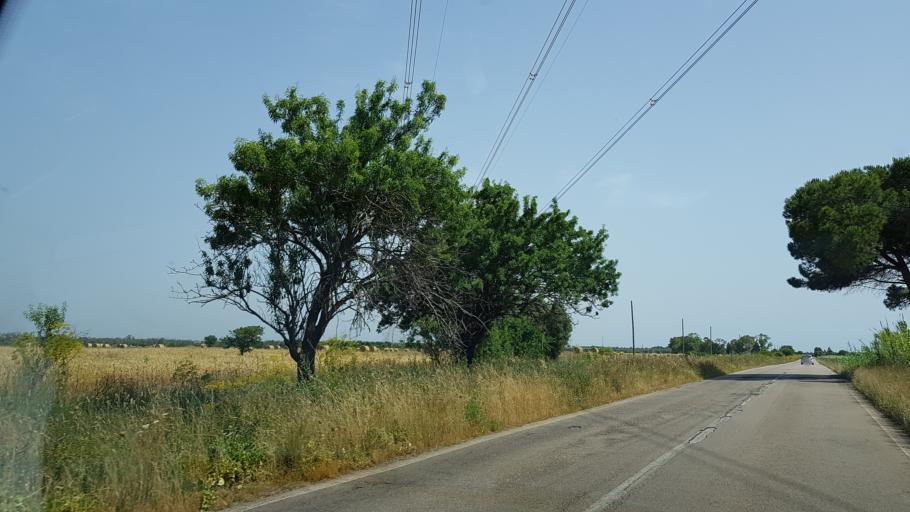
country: IT
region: Apulia
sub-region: Provincia di Brindisi
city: San Pancrazio Salentino
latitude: 40.3432
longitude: 17.8480
